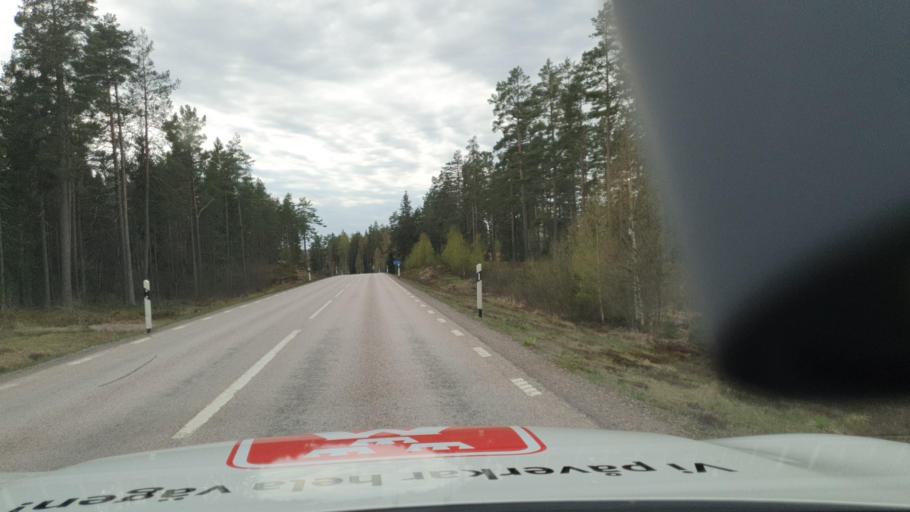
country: SE
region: Gaevleborg
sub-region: Gavle Kommun
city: Hedesunda
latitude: 60.4160
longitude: 17.0536
